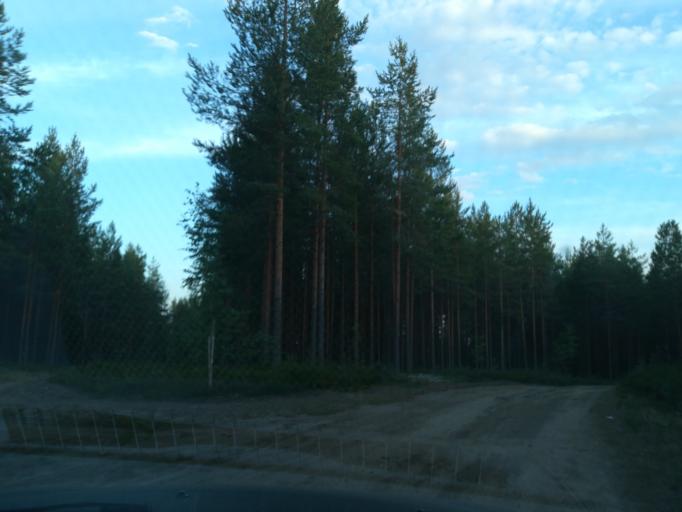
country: FI
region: South Karelia
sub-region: Lappeenranta
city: Joutseno
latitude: 61.3403
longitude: 28.4062
